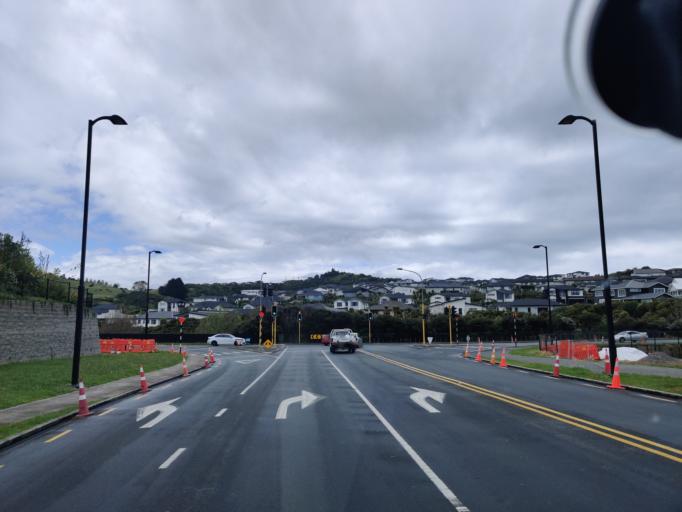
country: NZ
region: Auckland
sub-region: Auckland
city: Rothesay Bay
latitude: -36.5898
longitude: 174.6717
